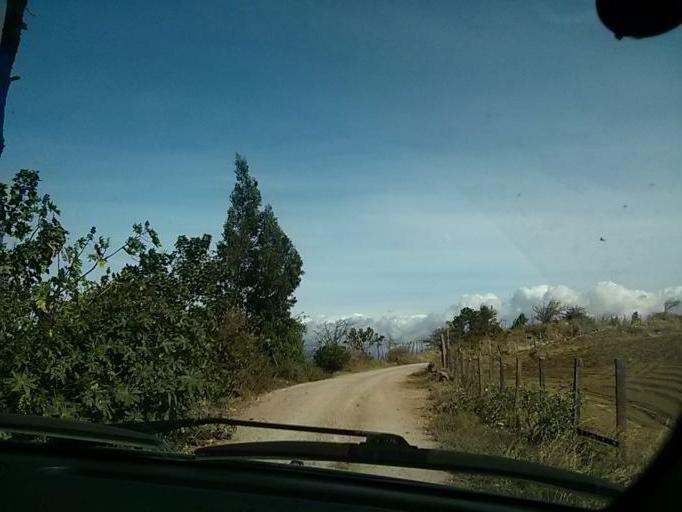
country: CR
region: Cartago
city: Cot
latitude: 9.9163
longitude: -83.9081
